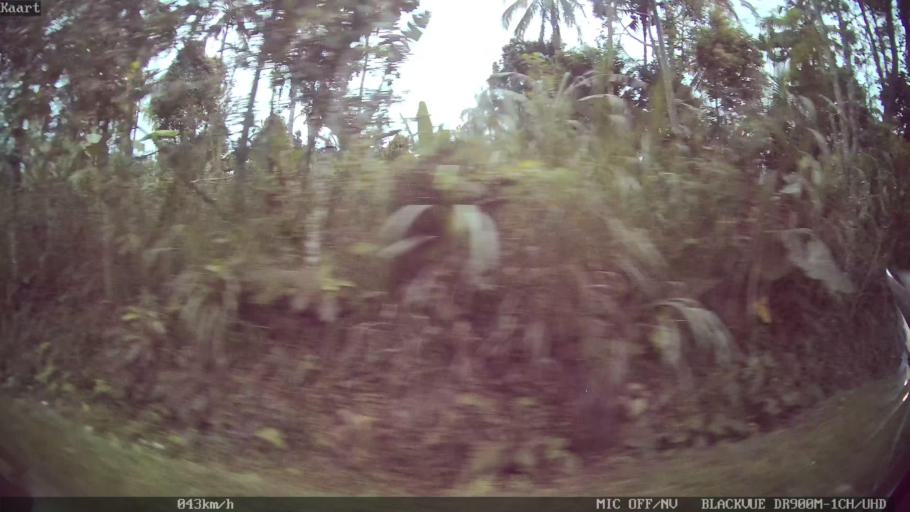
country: ID
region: Bali
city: Banjar Geriana Kangin
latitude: -8.3995
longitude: 115.4403
